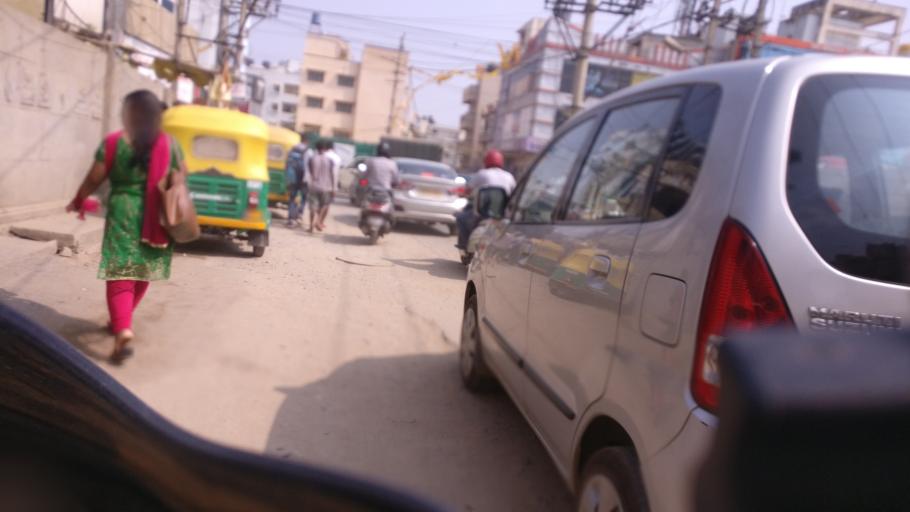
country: IN
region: Karnataka
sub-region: Bangalore Urban
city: Bangalore
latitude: 12.9135
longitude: 77.6773
